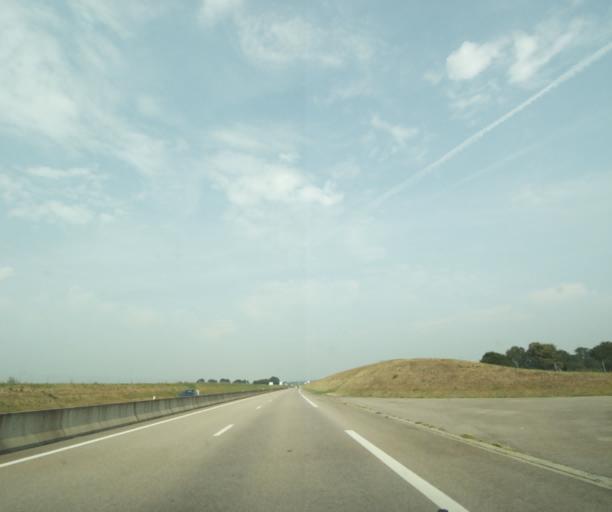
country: FR
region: Lower Normandy
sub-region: Departement du Calvados
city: Falaise
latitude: 48.8661
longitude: -0.2004
